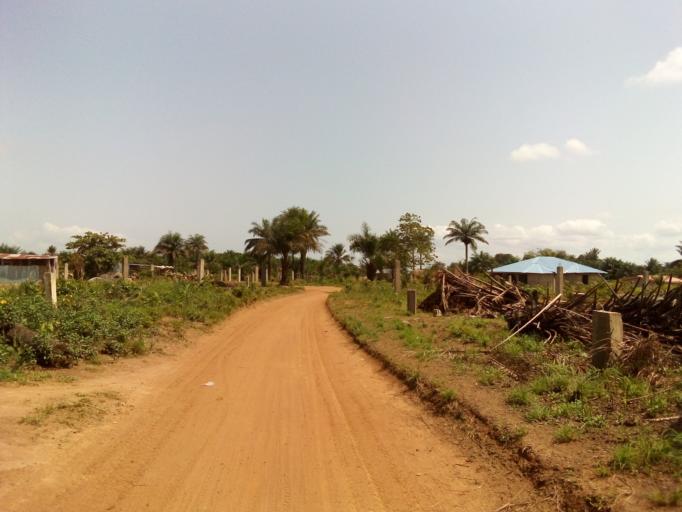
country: SL
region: Western Area
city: Waterloo
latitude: 8.3421
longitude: -13.0114
